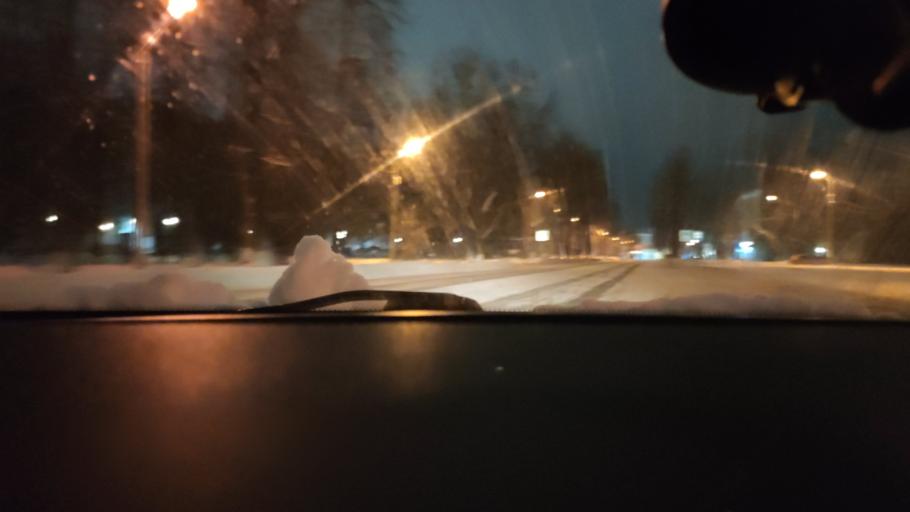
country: RU
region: Perm
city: Krasnokamsk
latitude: 58.0799
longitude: 55.7503
